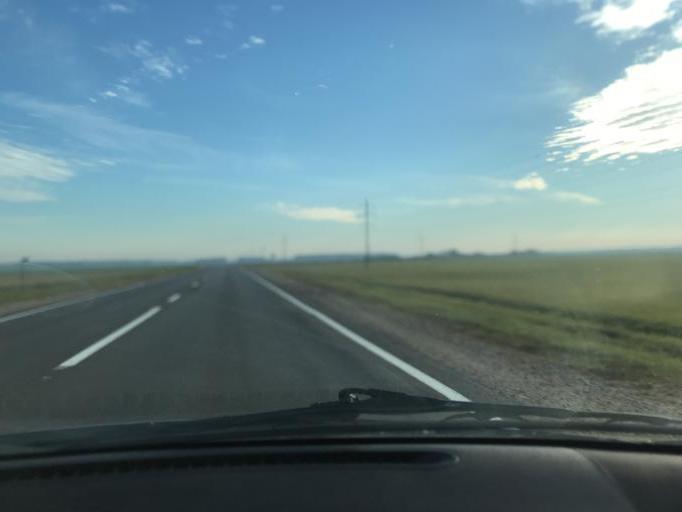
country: BY
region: Brest
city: Drahichyn
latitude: 52.2001
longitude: 25.0418
